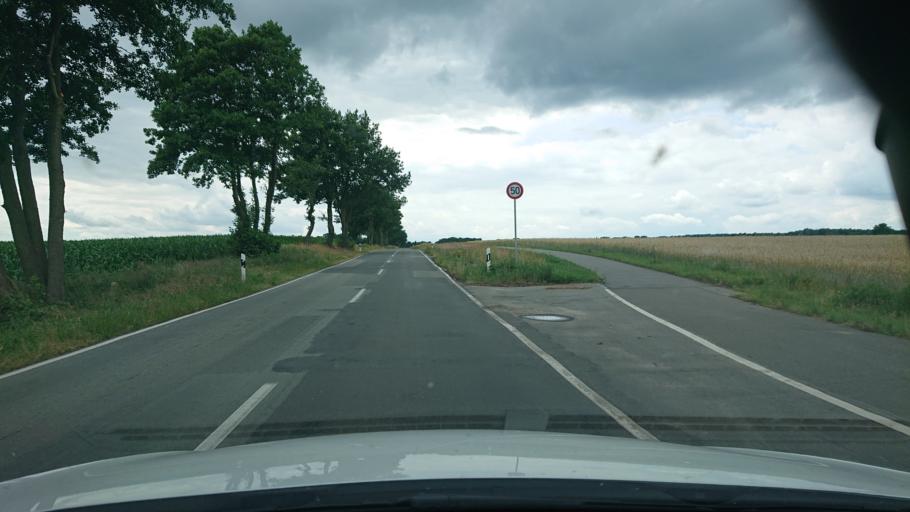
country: DE
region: Mecklenburg-Vorpommern
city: Ludwigslust
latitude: 53.3386
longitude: 11.4012
